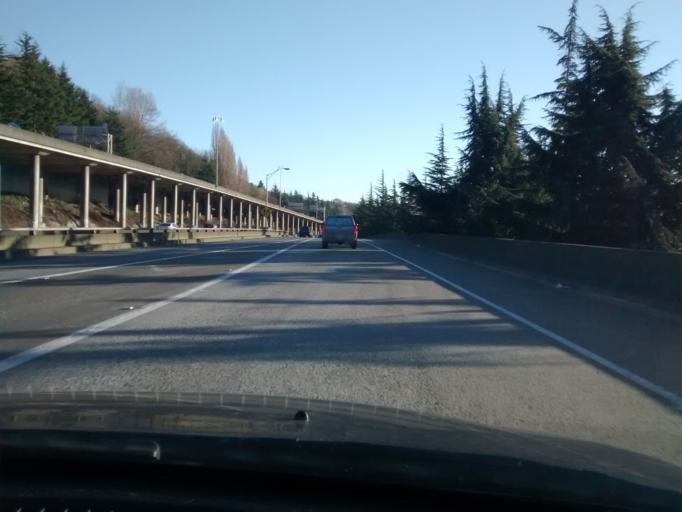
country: US
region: Washington
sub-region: King County
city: Seattle
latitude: 47.5905
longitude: -122.3215
